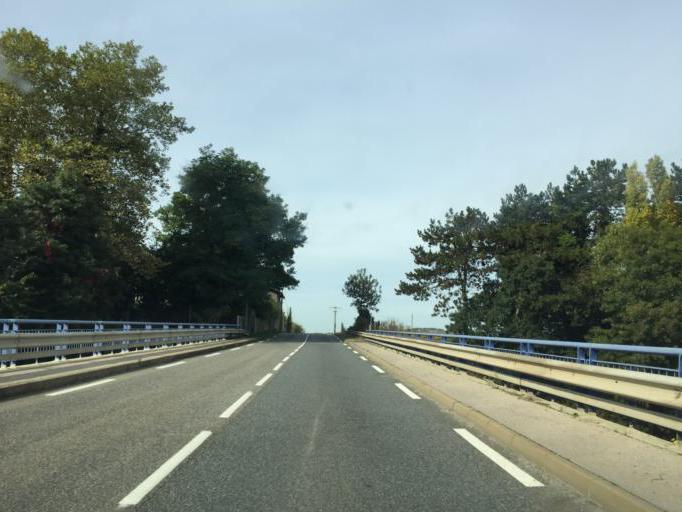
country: FR
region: Rhone-Alpes
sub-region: Departement du Rhone
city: Lissieu
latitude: 45.8707
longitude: 4.7409
